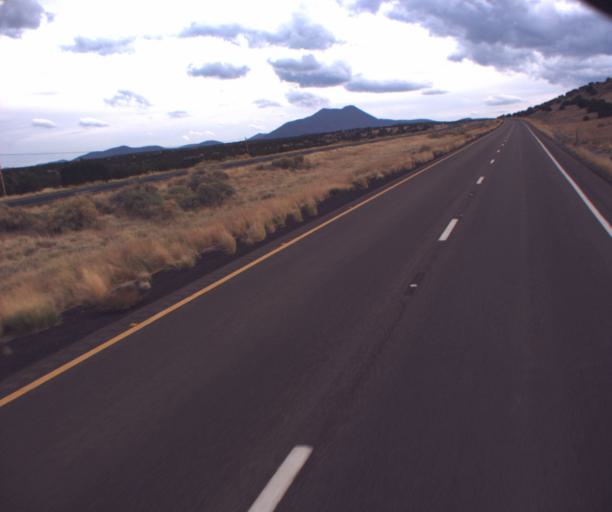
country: US
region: Arizona
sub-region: Coconino County
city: Flagstaff
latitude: 35.5249
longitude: -111.5430
